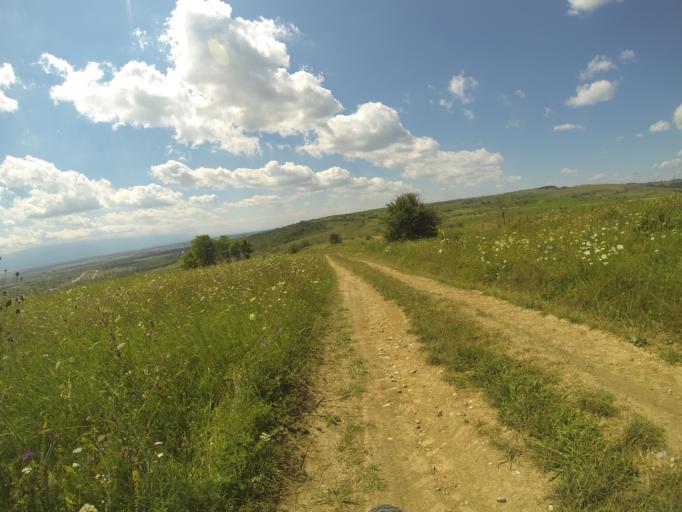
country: RO
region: Brasov
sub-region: Comuna Mandra
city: Mandra
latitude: 45.8572
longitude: 25.0657
